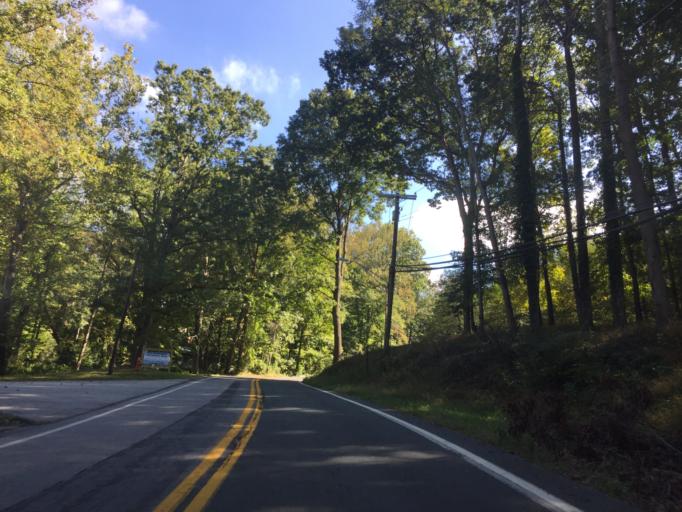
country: US
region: Maryland
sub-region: Baltimore County
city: Carney
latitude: 39.4204
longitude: -76.5280
